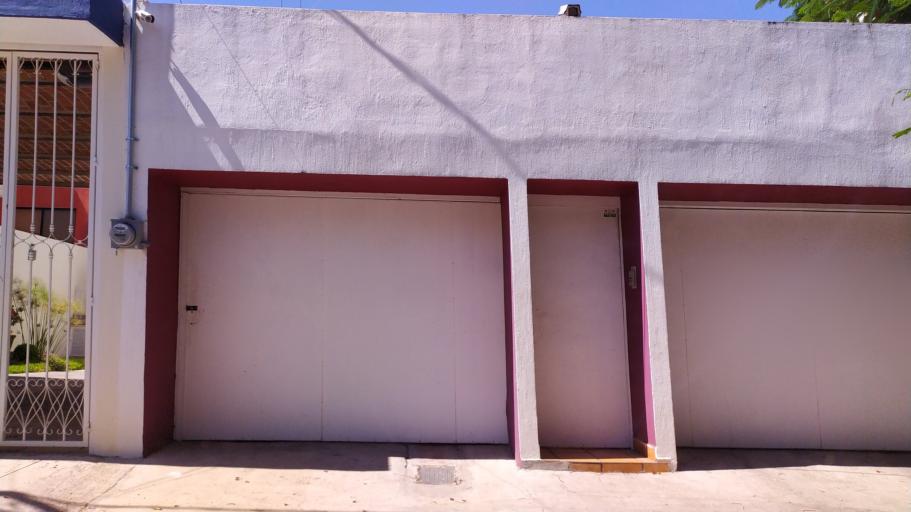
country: MX
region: Jalisco
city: Guadalajara
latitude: 20.6726
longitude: -103.3931
